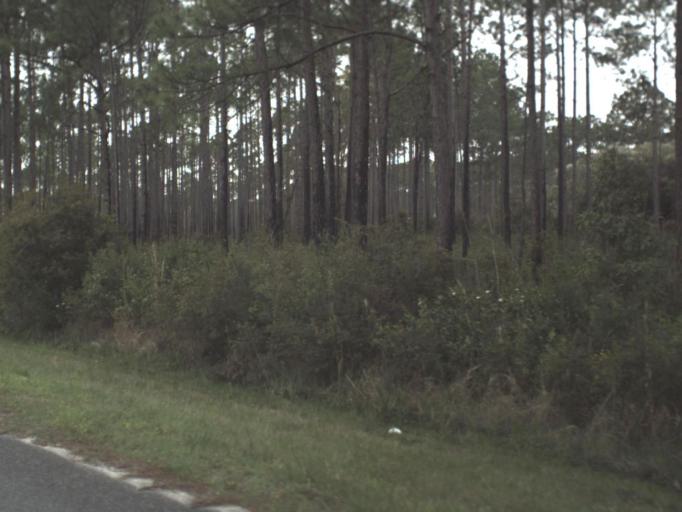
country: US
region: Florida
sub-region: Franklin County
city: Eastpoint
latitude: 29.7842
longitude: -84.8314
